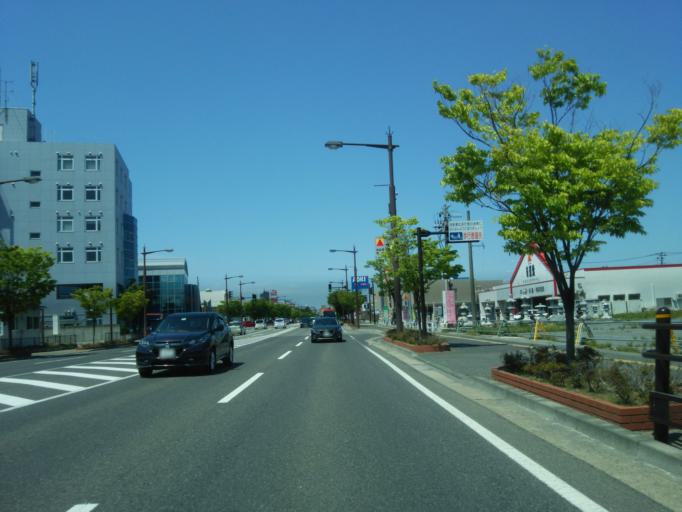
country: JP
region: Niigata
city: Kameda-honcho
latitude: 37.8911
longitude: 139.0700
